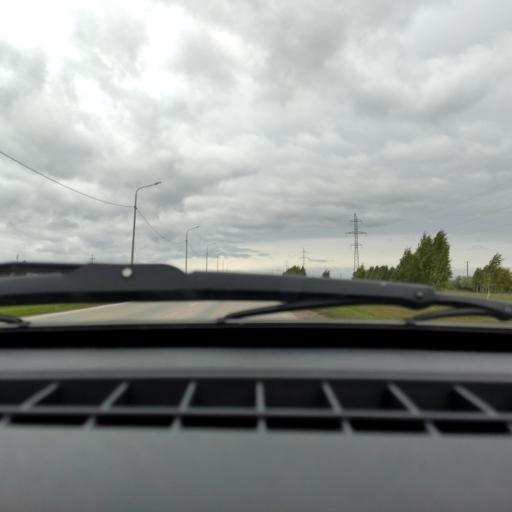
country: RU
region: Bashkortostan
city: Rayevskiy
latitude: 54.0595
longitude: 54.9124
